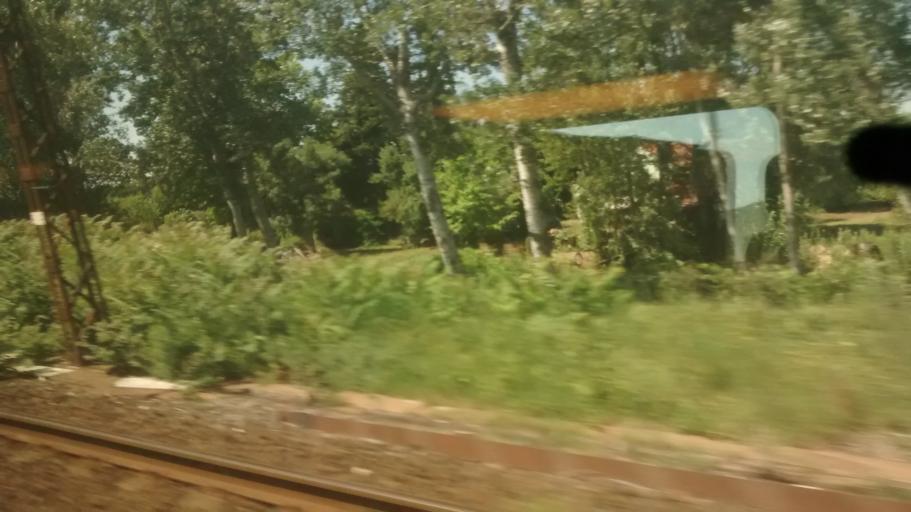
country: FR
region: Languedoc-Roussillon
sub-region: Departement de l'Herault
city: Lunel
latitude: 43.6798
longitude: 4.1190
